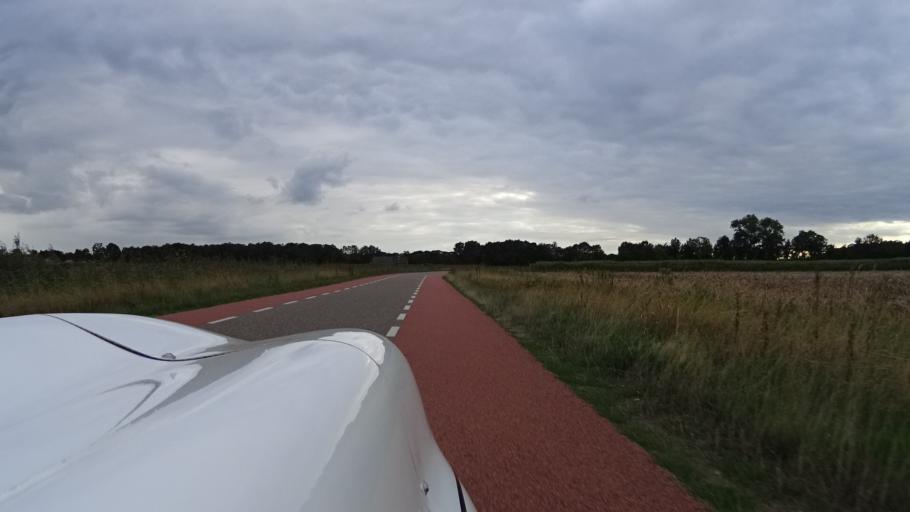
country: NL
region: North Brabant
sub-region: Gemeente Bernheze
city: Loosbroek
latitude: 51.6909
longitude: 5.4752
